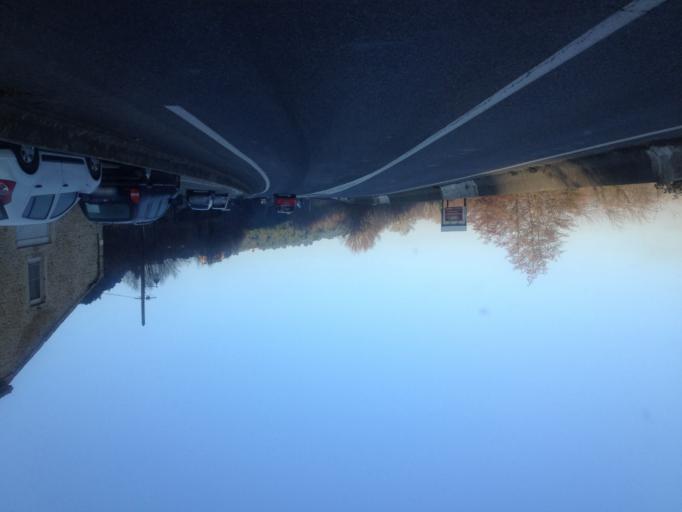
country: FR
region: Provence-Alpes-Cote d'Azur
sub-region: Departement du Vaucluse
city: Mornas
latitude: 44.2063
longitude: 4.7271
